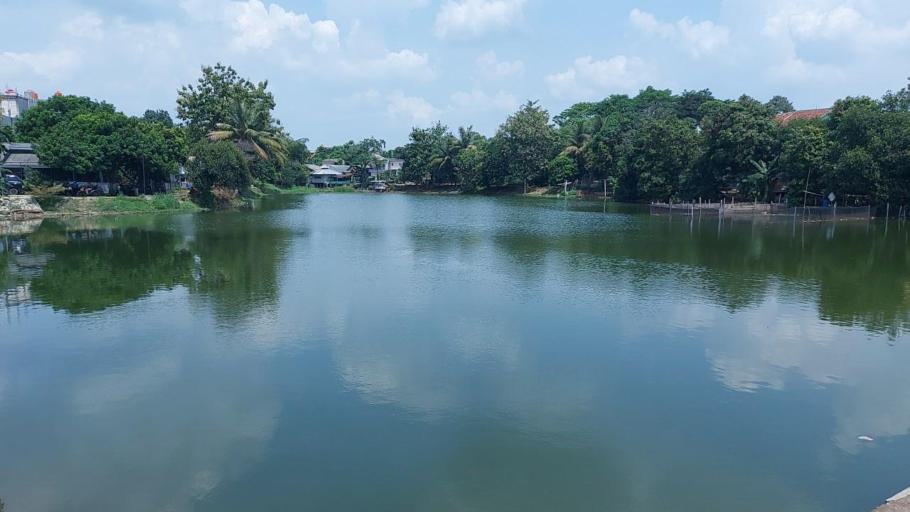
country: ID
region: West Java
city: Cibinong
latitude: -6.4706
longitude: 106.8484
